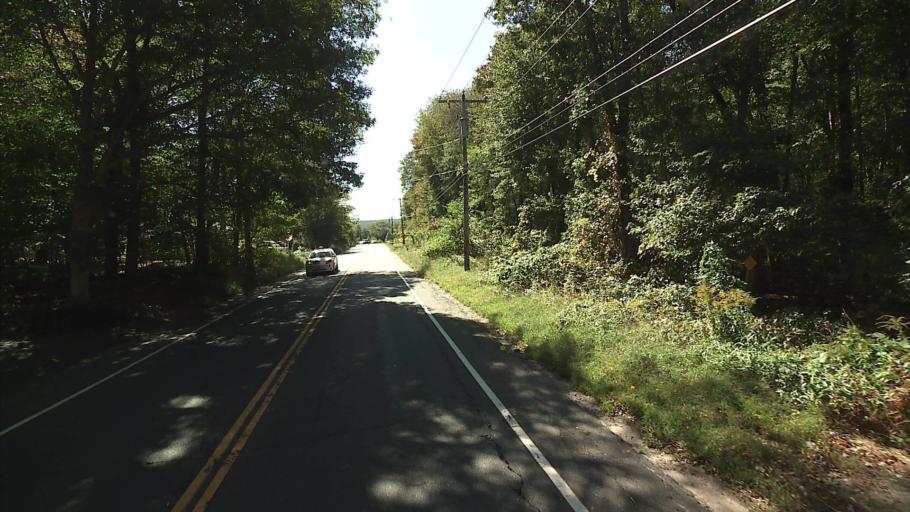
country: US
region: Connecticut
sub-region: New Haven County
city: Prospect
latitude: 41.4679
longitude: -72.9667
